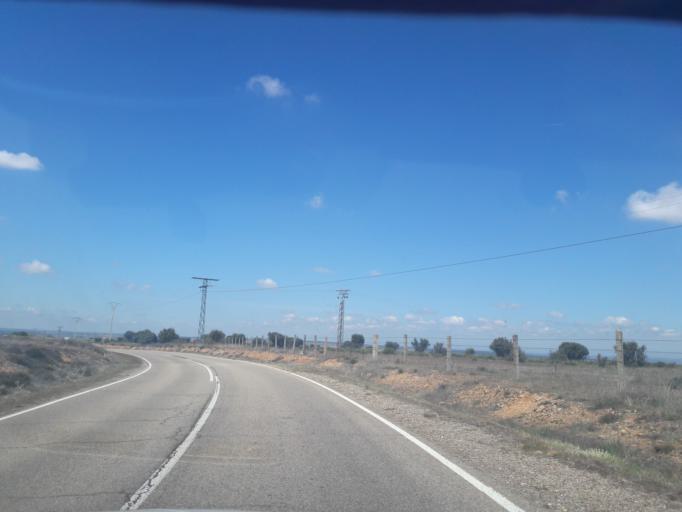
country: ES
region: Castille and Leon
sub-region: Provincia de Salamanca
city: Doninos de Salamanca
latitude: 40.9428
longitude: -5.7264
